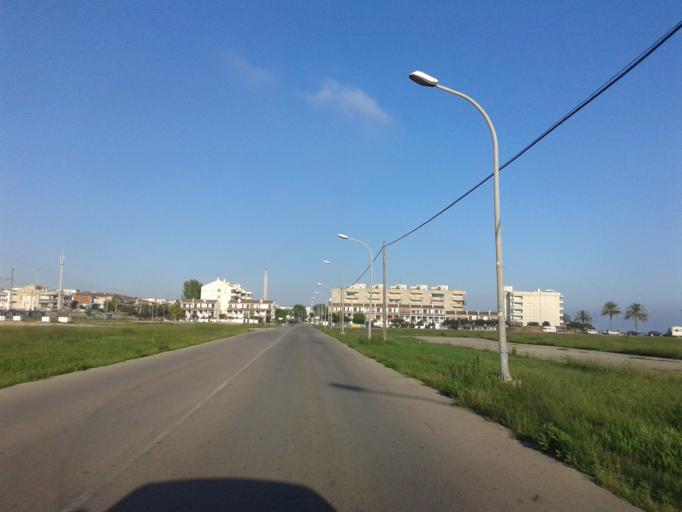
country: ES
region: Catalonia
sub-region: Provincia de Tarragona
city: Cunit
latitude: 41.1938
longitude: 1.6320
